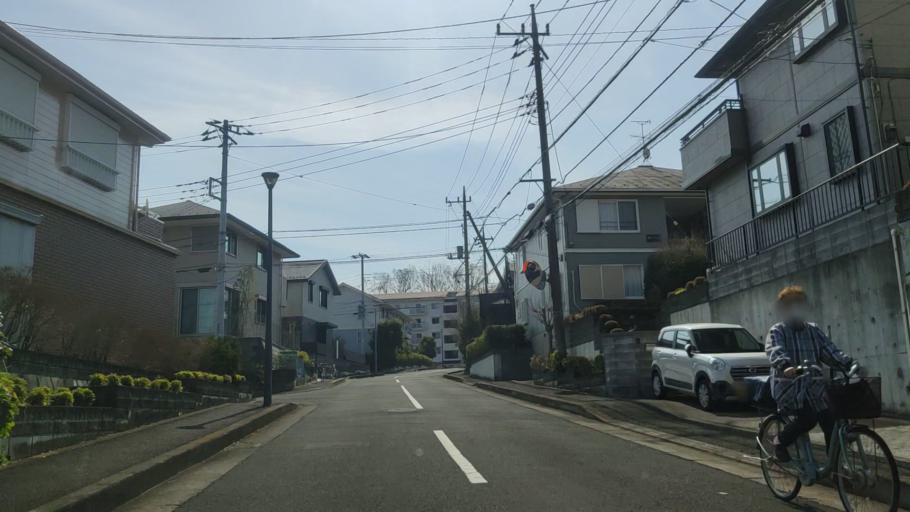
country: JP
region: Kanagawa
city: Isehara
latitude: 35.3875
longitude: 139.2736
